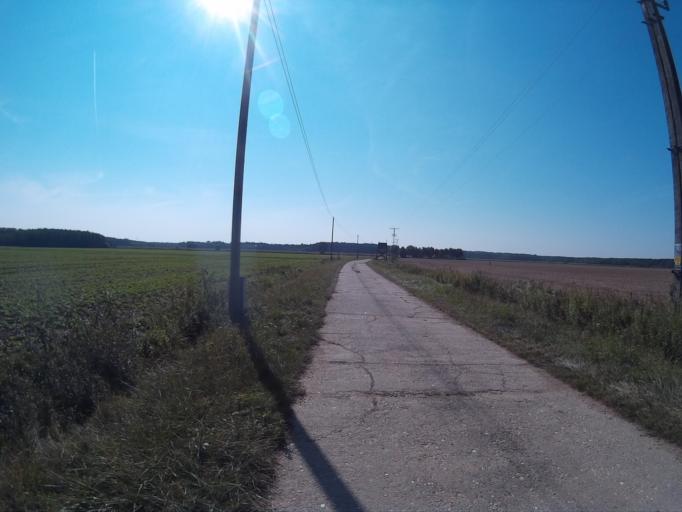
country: HU
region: Vas
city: Kormend
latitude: 47.0774
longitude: 16.6292
